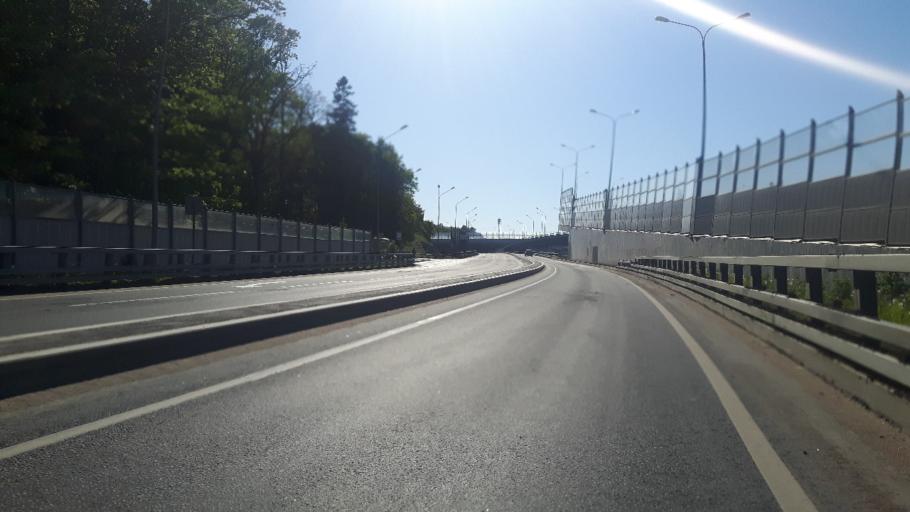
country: RU
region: St.-Petersburg
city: Lomonosov
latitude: 59.9265
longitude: 29.6766
